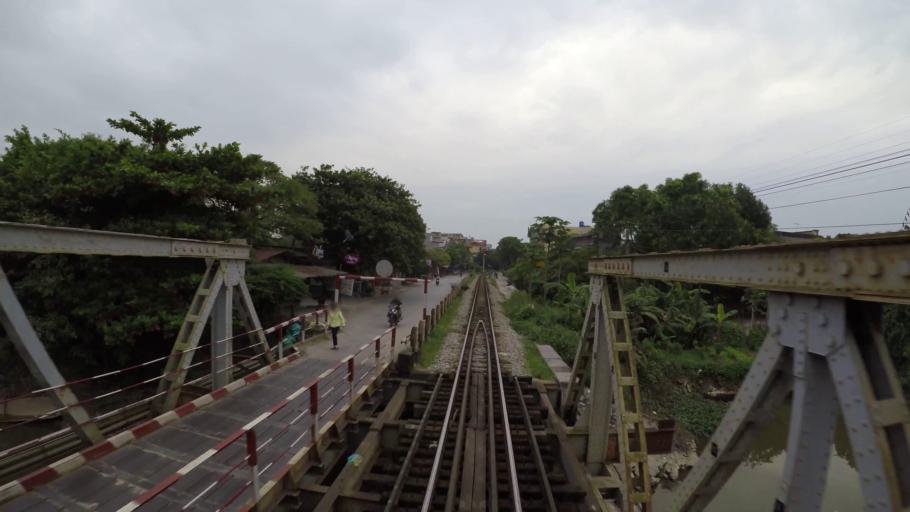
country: VN
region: Hai Duong
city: Ke Sat
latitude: 20.9662
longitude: 106.1420
